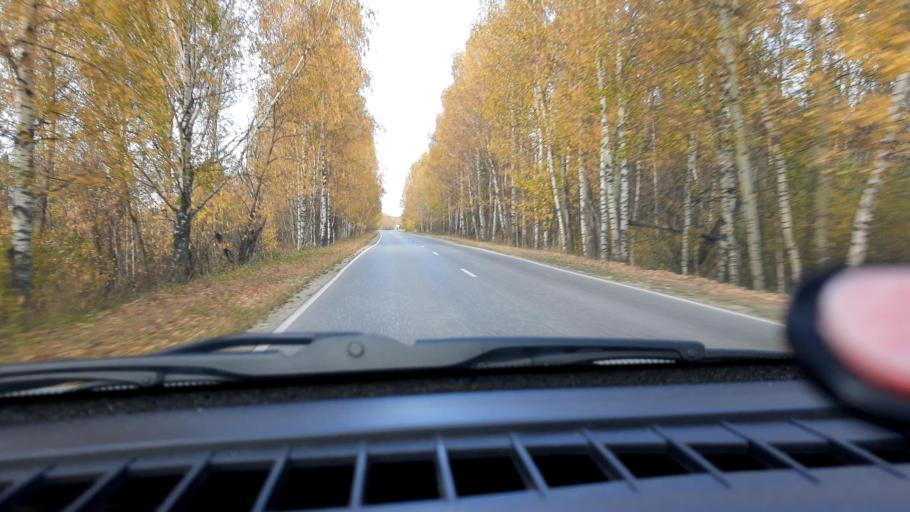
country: RU
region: Nizjnij Novgorod
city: Neklyudovo
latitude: 56.5224
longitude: 43.8351
